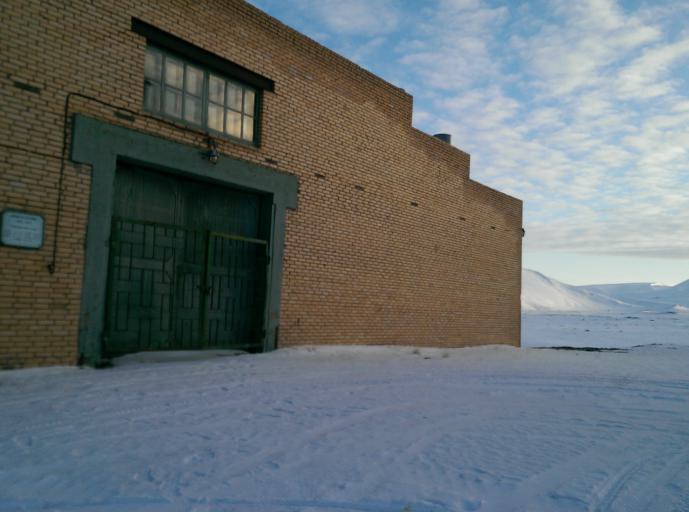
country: SJ
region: Svalbard
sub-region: Spitsbergen
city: Longyearbyen
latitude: 78.6543
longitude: 16.3187
